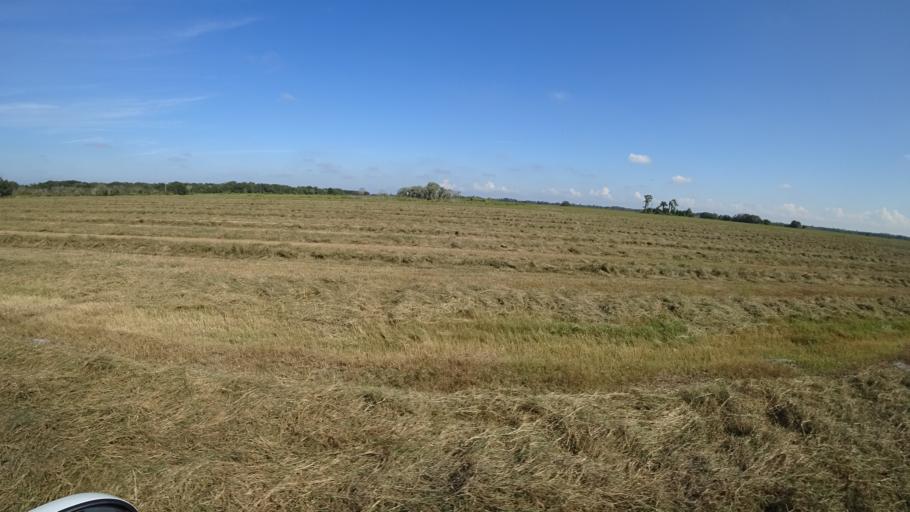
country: US
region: Florida
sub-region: DeSoto County
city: Nocatee
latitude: 27.2674
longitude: -82.0950
